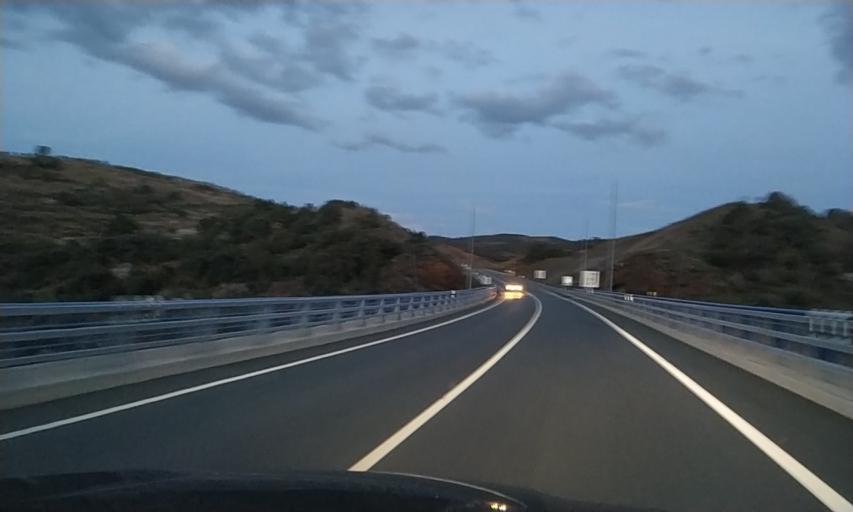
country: PT
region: Braganca
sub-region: Alfandega da Fe
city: Alfandega da Fe
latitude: 41.3074
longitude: -6.9181
